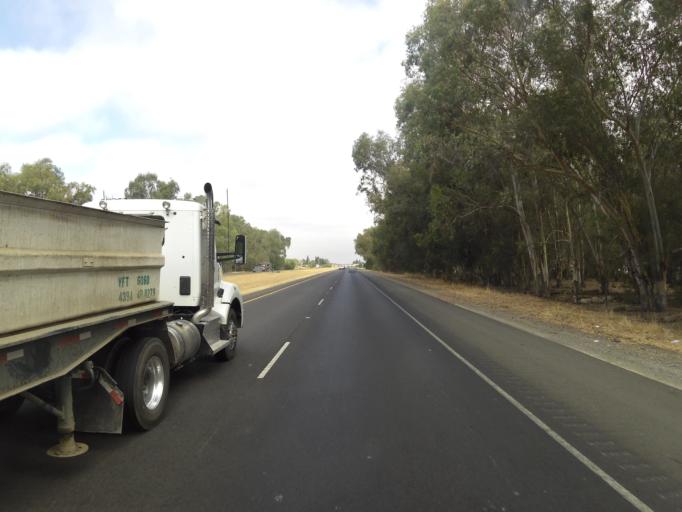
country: US
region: California
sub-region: Yolo County
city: Dunnigan
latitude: 38.8989
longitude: -121.9825
